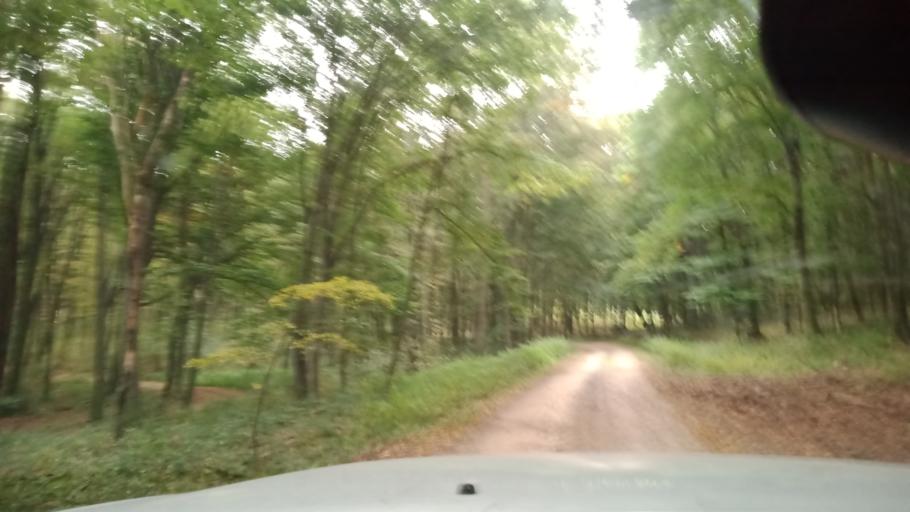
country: HU
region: Fejer
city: Mor
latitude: 47.3827
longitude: 18.2582
